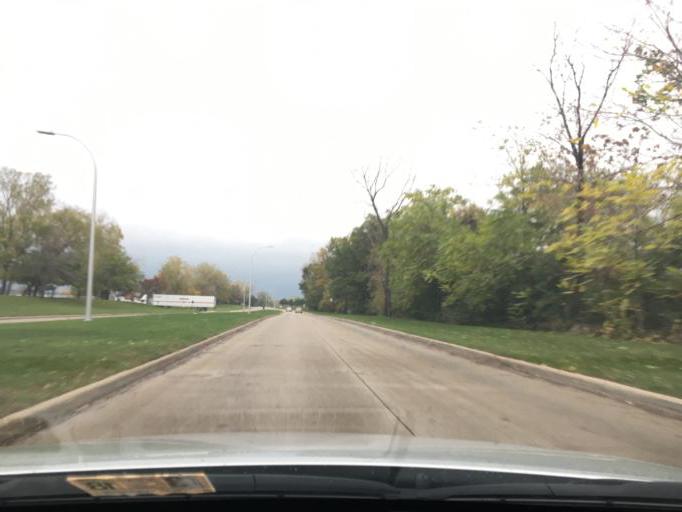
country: US
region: Michigan
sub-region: Wayne County
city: Melvindale
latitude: 42.2887
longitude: -83.2009
